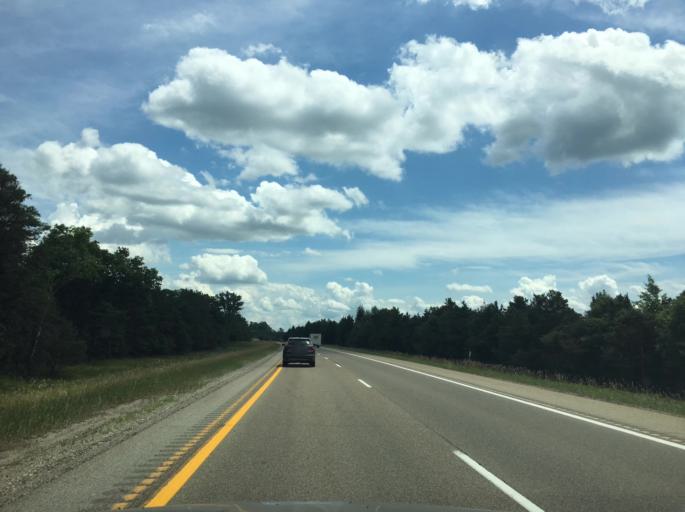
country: US
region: Michigan
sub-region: Roscommon County
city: Roscommon
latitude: 44.5444
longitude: -84.6984
